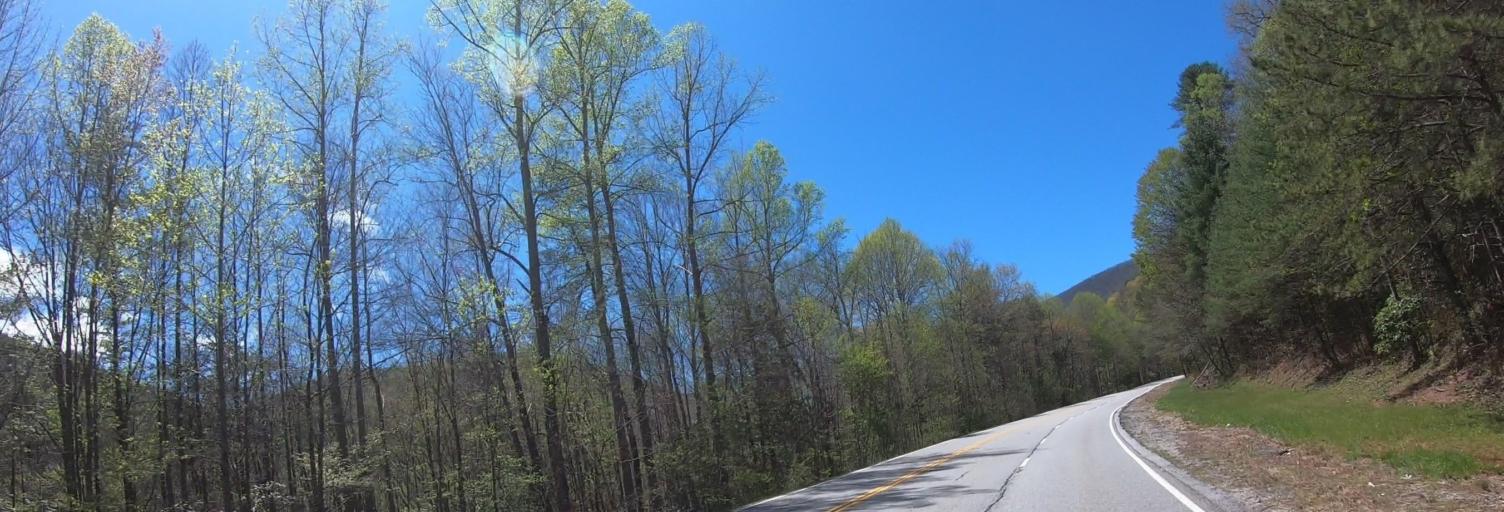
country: US
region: Georgia
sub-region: Towns County
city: Hiawassee
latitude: 34.8237
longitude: -83.7344
